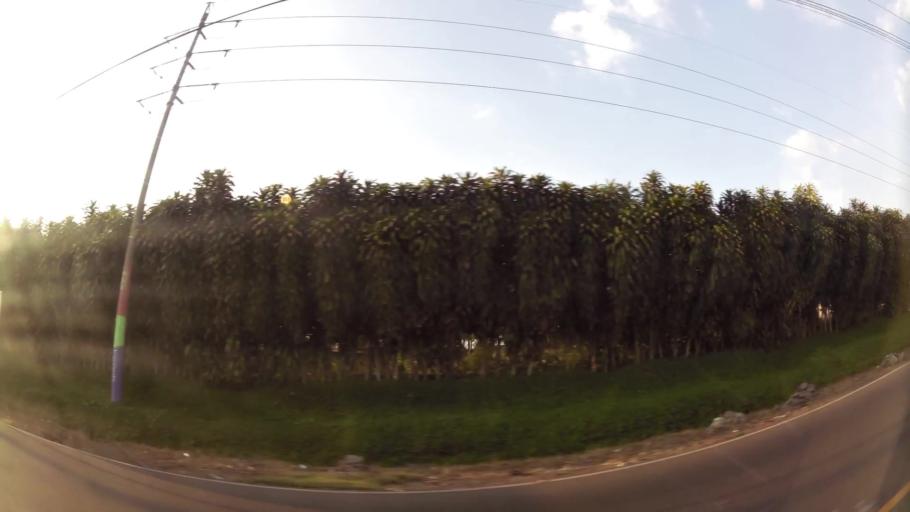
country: GT
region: Retalhuleu
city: San Sebastian
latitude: 14.5522
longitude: -91.6569
